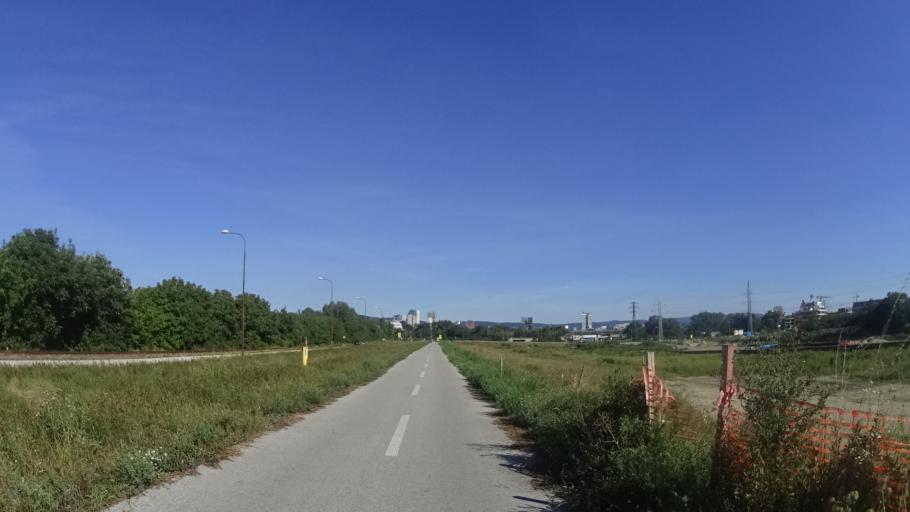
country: SK
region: Bratislavsky
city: Bratislava
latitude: 48.1347
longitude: 17.1540
